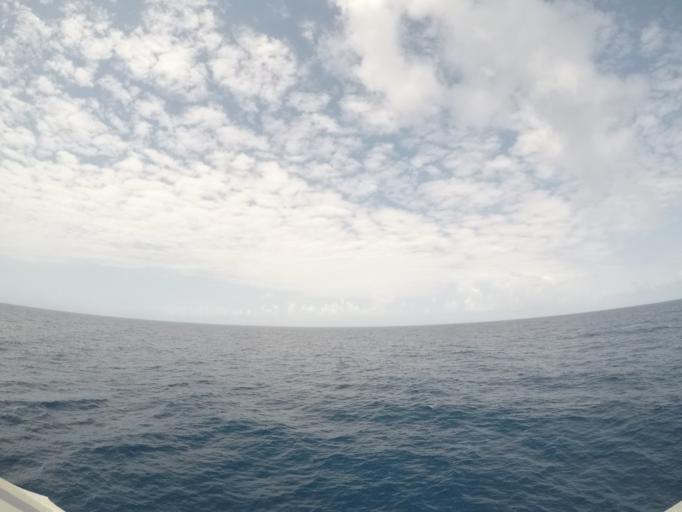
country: TZ
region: Zanzibar North
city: Nungwi
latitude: -5.5792
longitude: 39.3603
